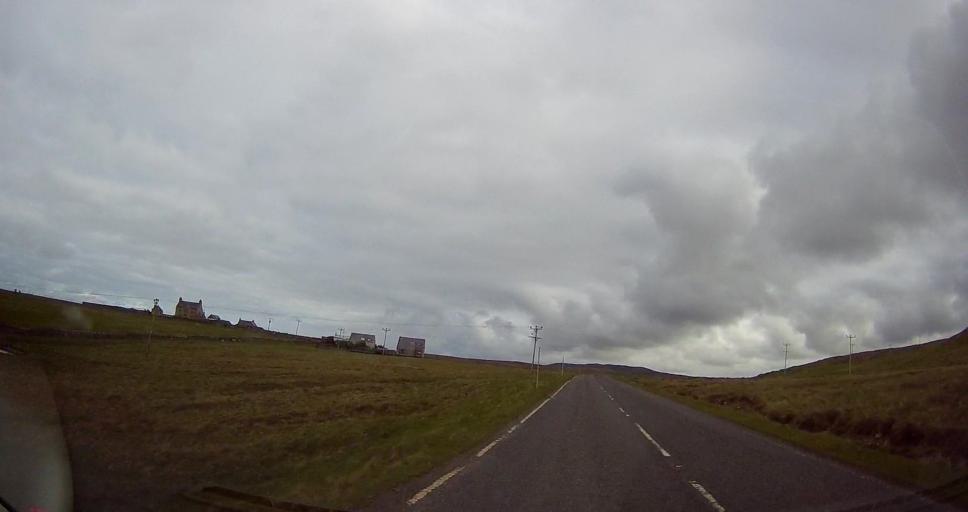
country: GB
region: Scotland
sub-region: Shetland Islands
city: Shetland
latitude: 60.6845
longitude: -0.9655
